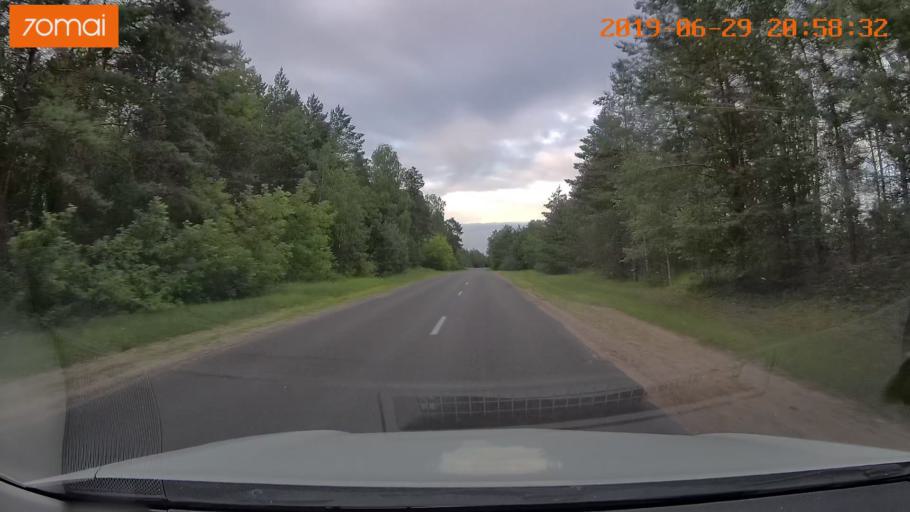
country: BY
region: Brest
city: Hantsavichy
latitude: 52.7306
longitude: 26.3879
